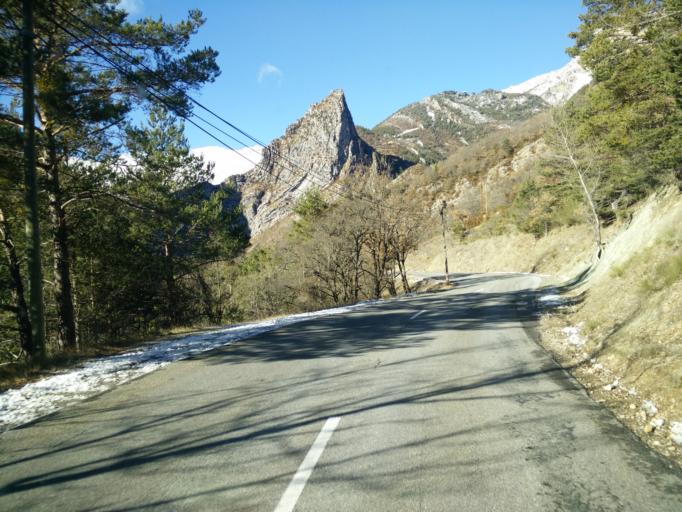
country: FR
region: Provence-Alpes-Cote d'Azur
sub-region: Departement des Alpes-de-Haute-Provence
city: Castellane
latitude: 43.8288
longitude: 6.4589
